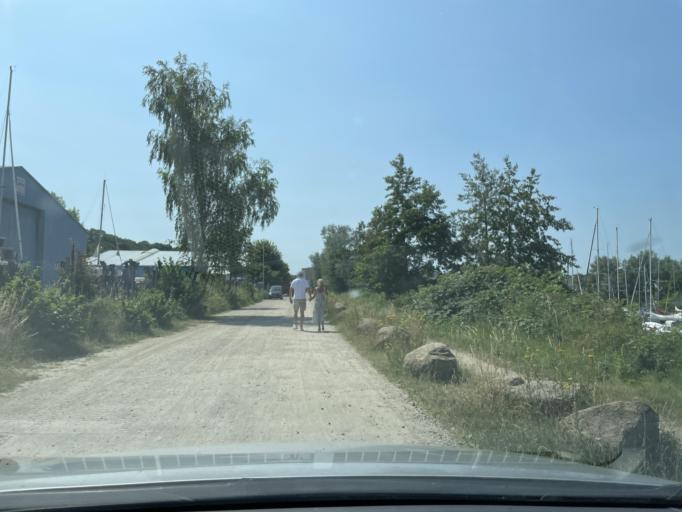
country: DE
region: Schleswig-Holstein
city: Flensburg
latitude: 54.8035
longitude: 9.4427
